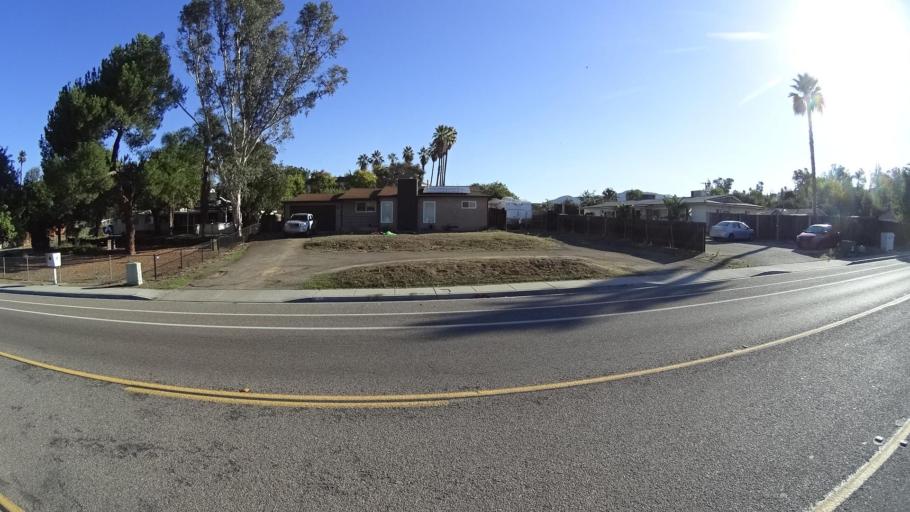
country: US
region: California
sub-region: San Diego County
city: Lakeside
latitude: 32.8367
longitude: -116.9084
